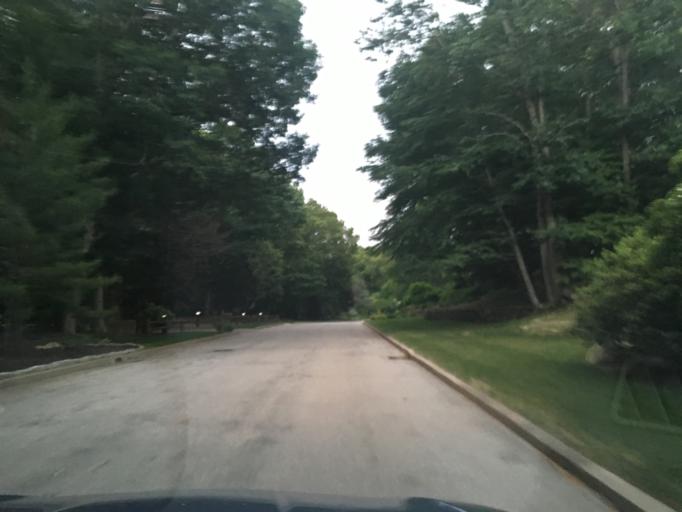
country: US
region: Rhode Island
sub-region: Washington County
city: Exeter
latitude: 41.6331
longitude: -71.5230
